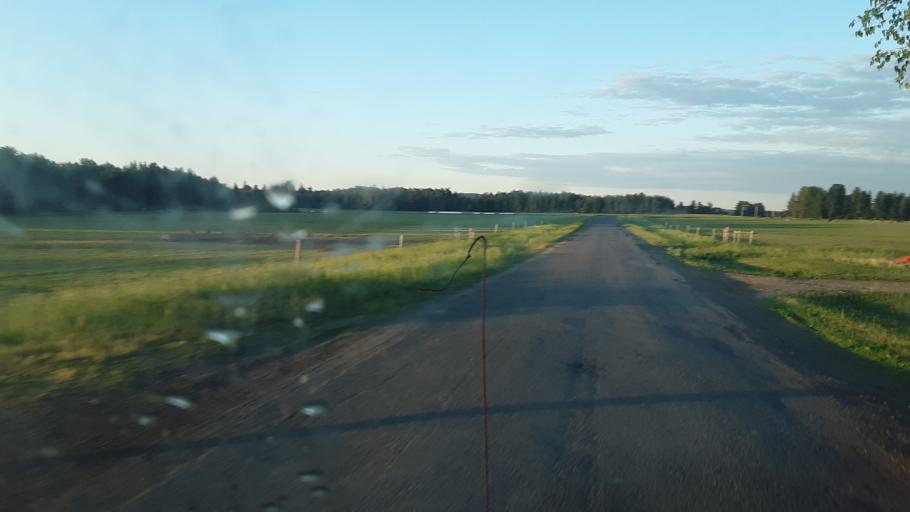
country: US
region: Maine
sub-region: Aroostook County
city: Caribou
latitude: 46.7917
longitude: -68.0977
